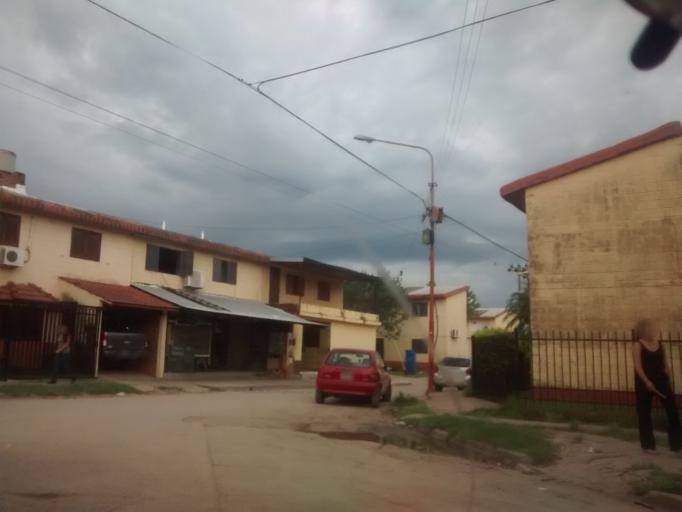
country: AR
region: Chaco
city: Fontana
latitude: -27.4438
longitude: -59.0172
